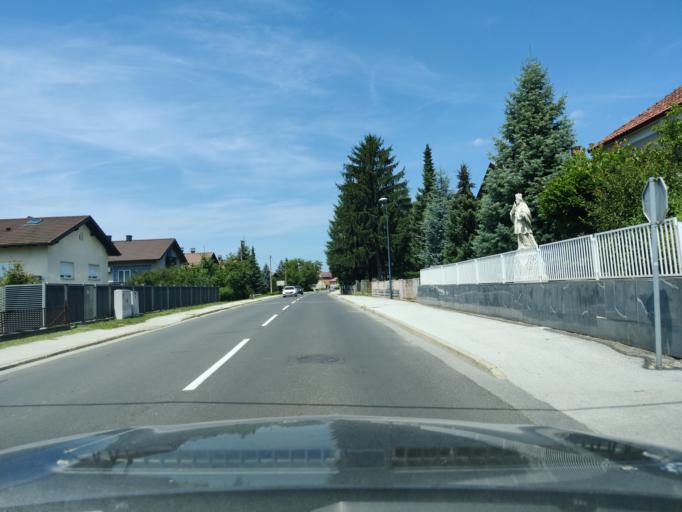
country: SI
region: Lendava-Lendva
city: Lendava
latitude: 46.5739
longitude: 16.4477
